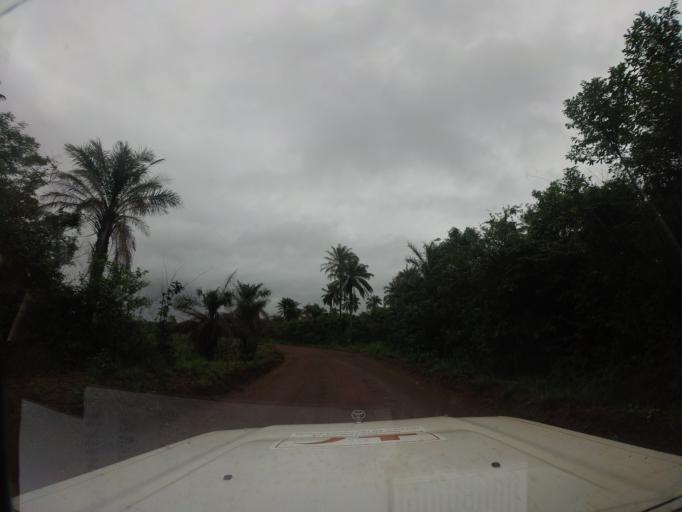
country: SL
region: Northern Province
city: Kambia
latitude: 9.1532
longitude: -12.8779
